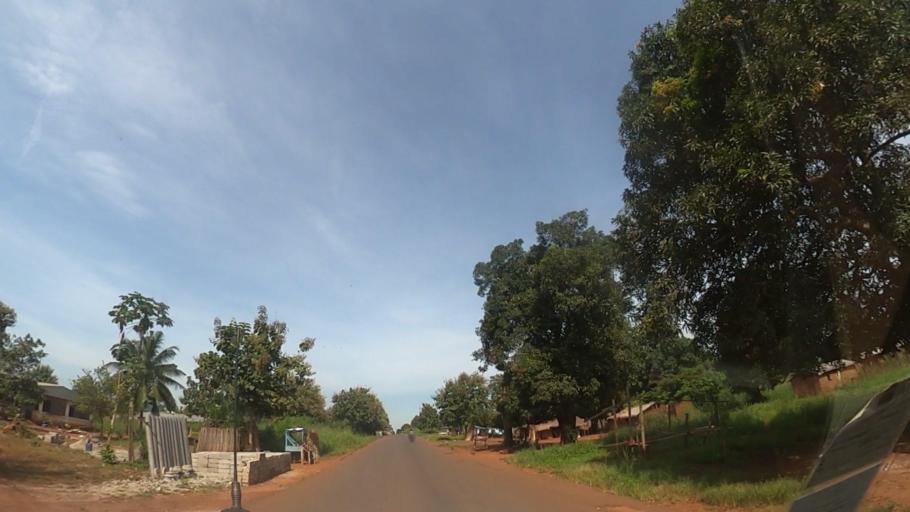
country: CF
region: Ombella-Mpoko
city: Bimbo
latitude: 4.3127
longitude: 18.4764
